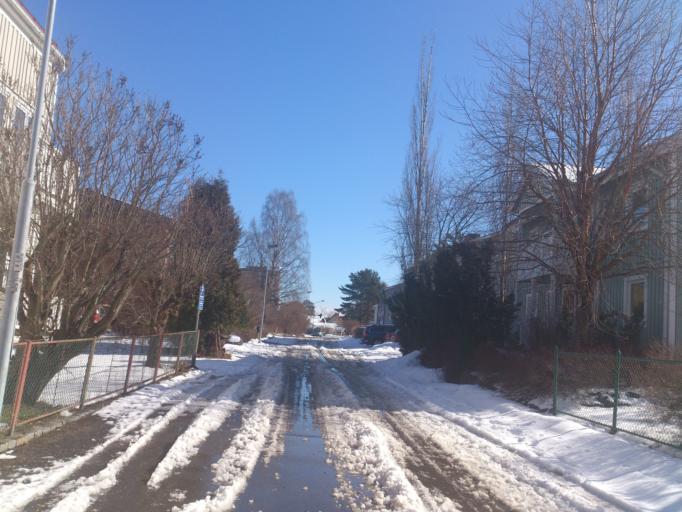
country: SE
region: Vaesternorrland
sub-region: Sundsvalls Kommun
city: Sundsvall
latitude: 62.3799
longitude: 17.3286
